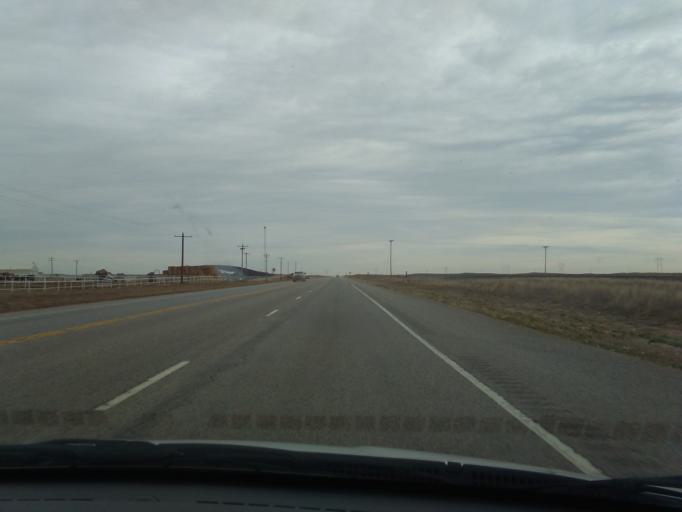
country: US
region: Colorado
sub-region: Morgan County
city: Brush
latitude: 40.2604
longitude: -103.5383
